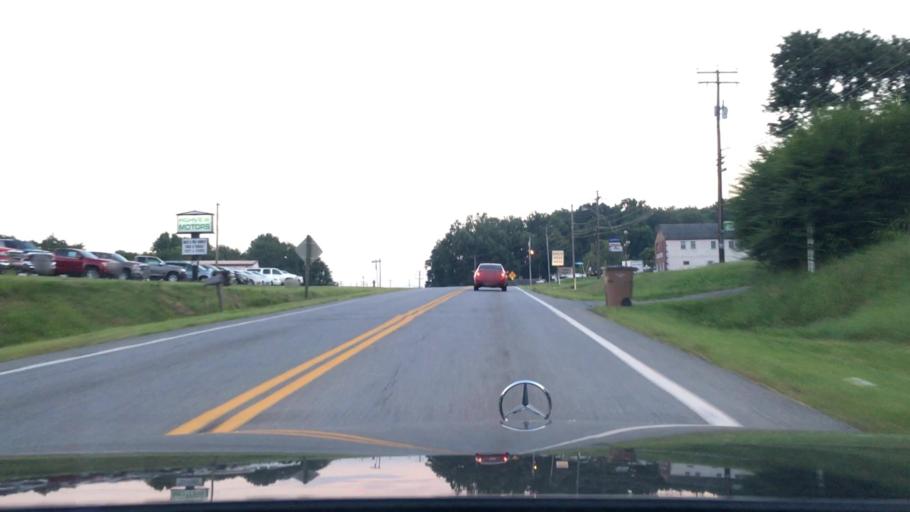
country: US
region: Virginia
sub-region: Campbell County
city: Altavista
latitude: 37.1250
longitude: -79.2722
